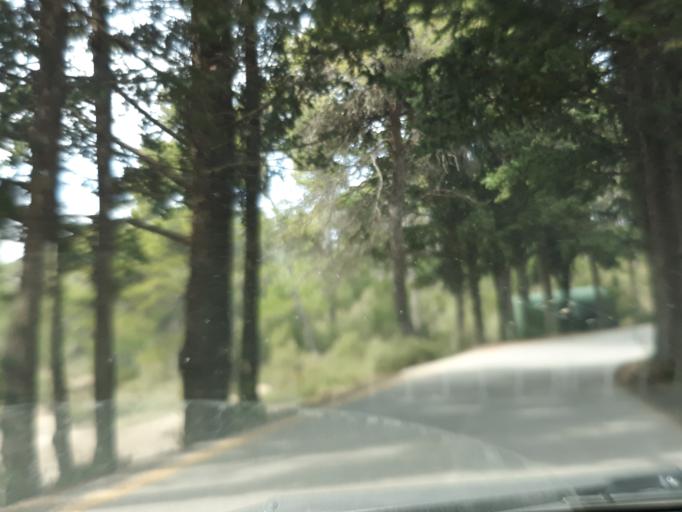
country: GR
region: Attica
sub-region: Nomarchia Anatolikis Attikis
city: Varybobi
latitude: 38.1607
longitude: 23.7875
